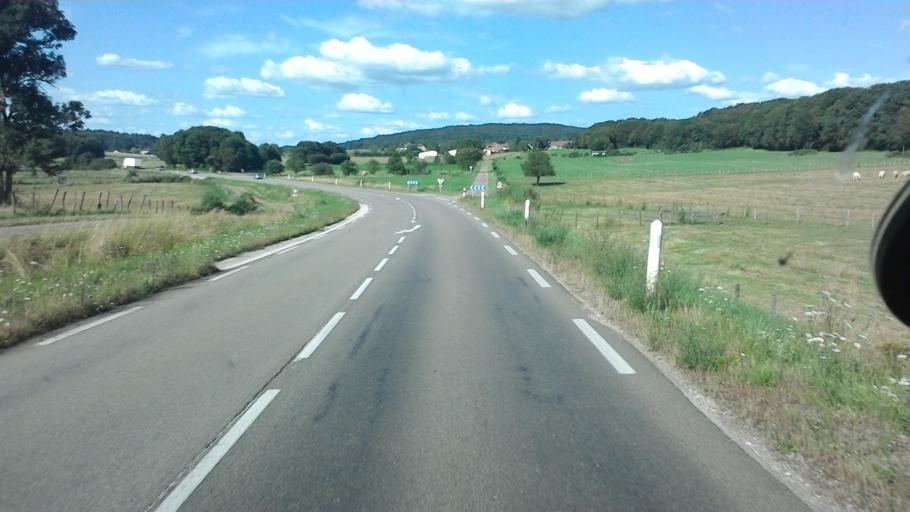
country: FR
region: Franche-Comte
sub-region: Departement de la Haute-Saone
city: Noidans-les-Vesoul
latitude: 47.5753
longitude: 6.0911
